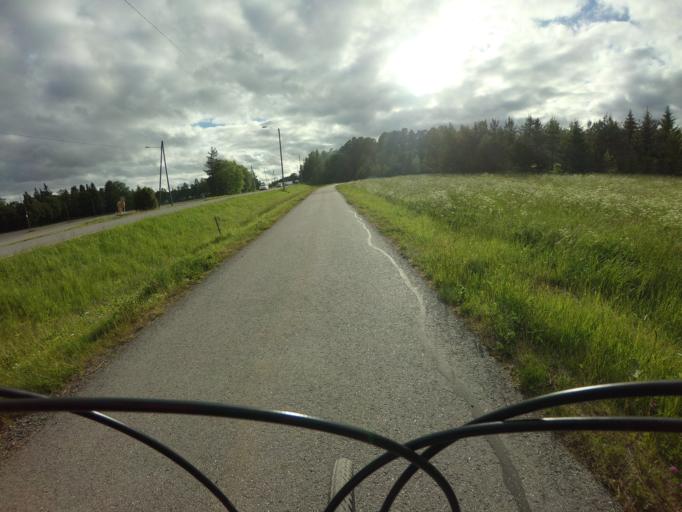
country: FI
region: Varsinais-Suomi
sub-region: Turku
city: Turku
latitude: 60.4959
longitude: 22.3462
